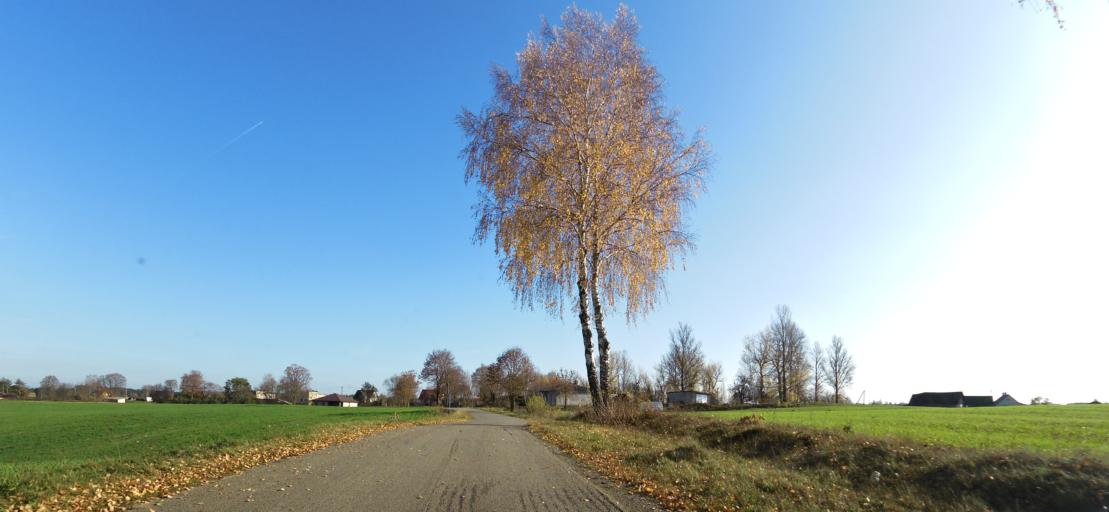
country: LT
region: Vilnius County
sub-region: Vilniaus Rajonas
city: Vievis
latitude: 54.6476
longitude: 24.7394
